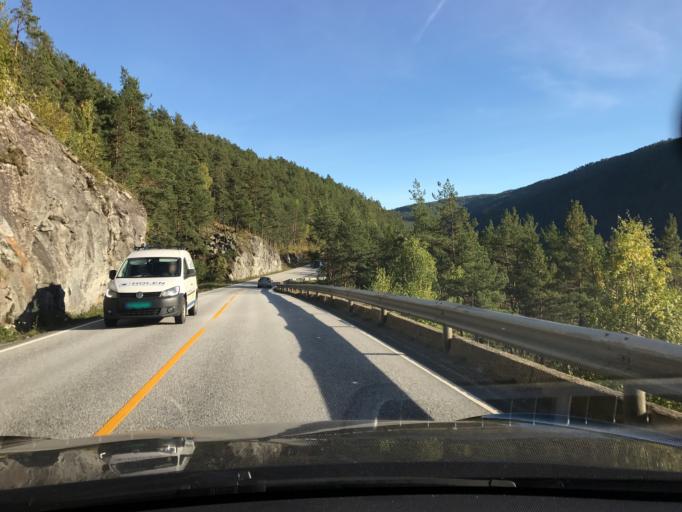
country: NO
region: Sogn og Fjordane
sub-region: Sogndal
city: Sogndalsfjora
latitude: 61.2100
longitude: 7.1532
